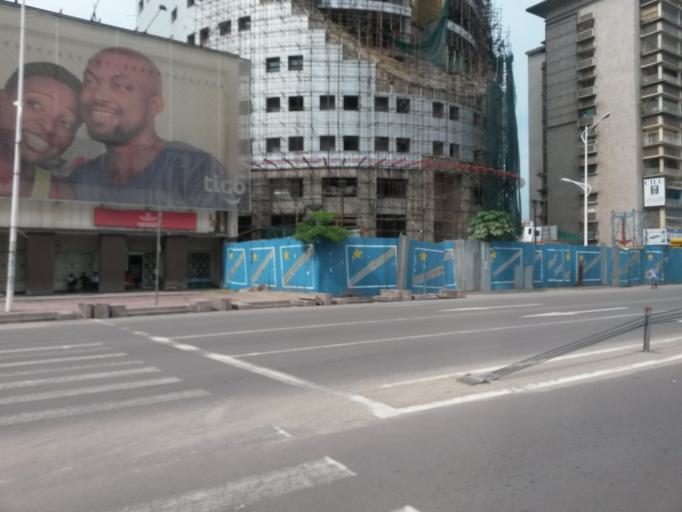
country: CD
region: Kinshasa
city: Kinshasa
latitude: -4.3043
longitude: 15.3069
